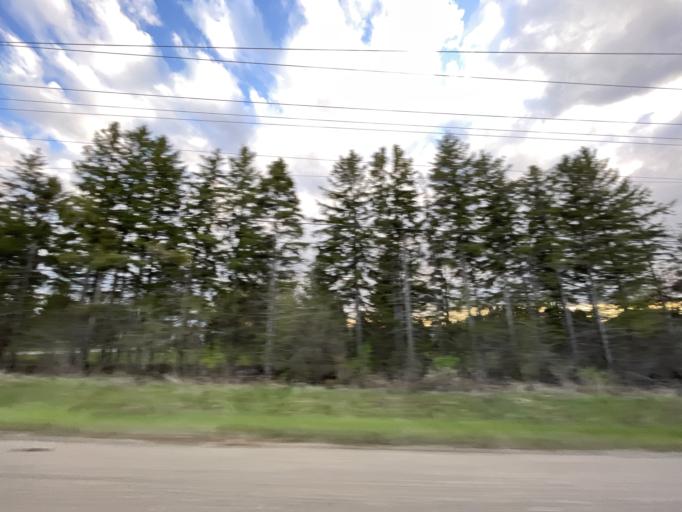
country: CA
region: Ontario
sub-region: Wellington County
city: Guelph
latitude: 43.5955
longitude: -80.2844
